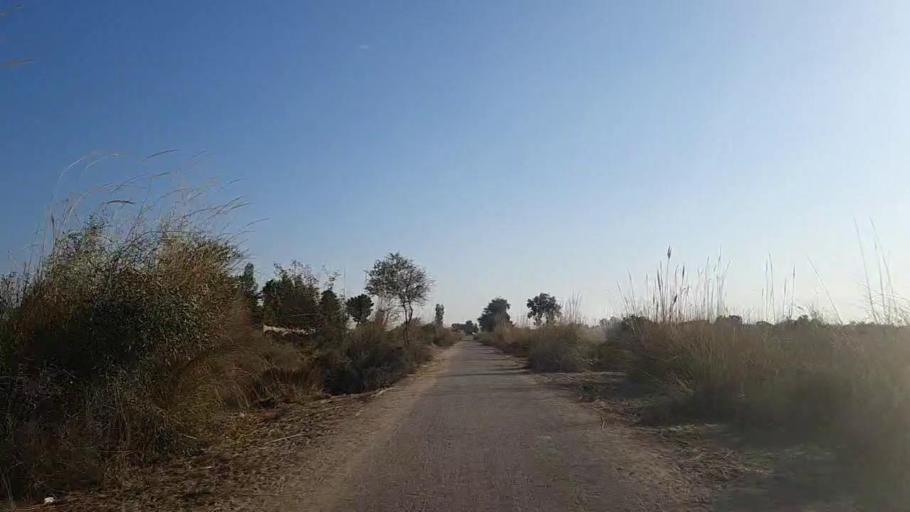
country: PK
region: Sindh
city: Khadro
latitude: 26.2787
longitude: 68.8603
